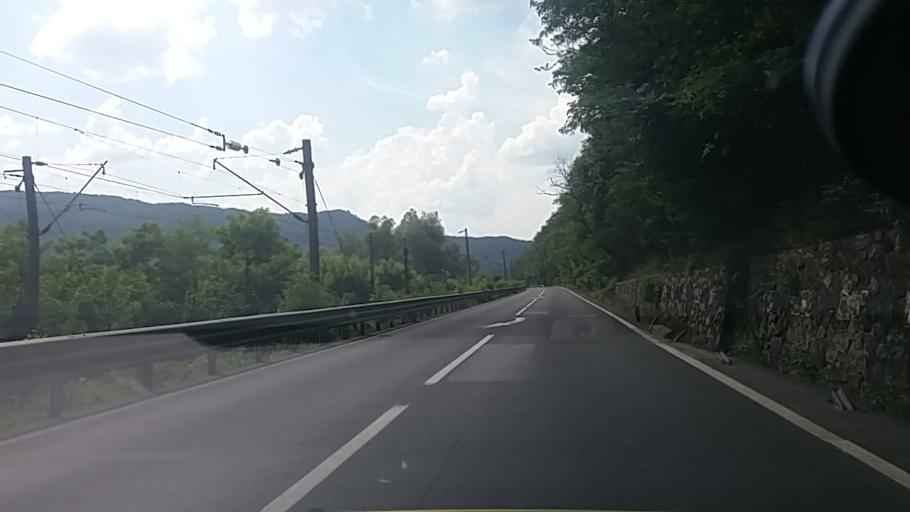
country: RO
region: Hunedoara
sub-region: Comuna Zam
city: Zam
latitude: 45.9730
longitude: 22.4469
